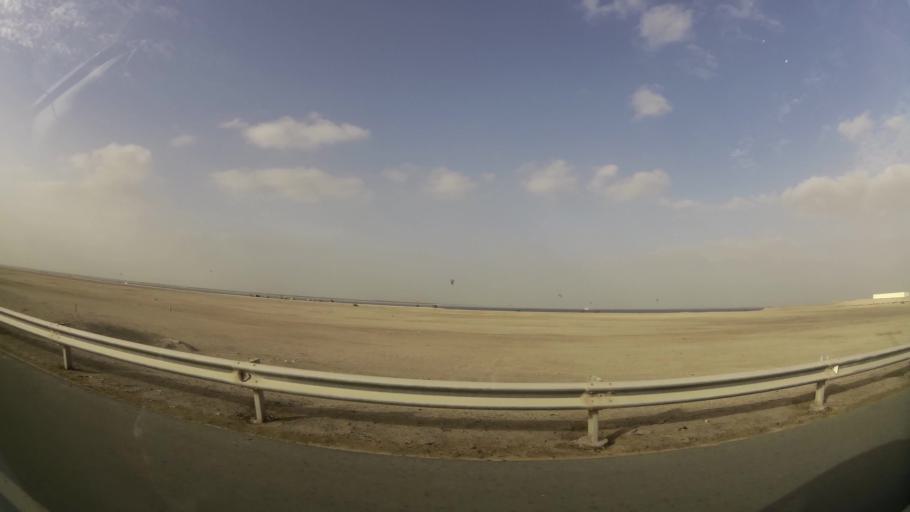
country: AE
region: Abu Dhabi
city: Abu Dhabi
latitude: 24.5065
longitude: 54.5657
